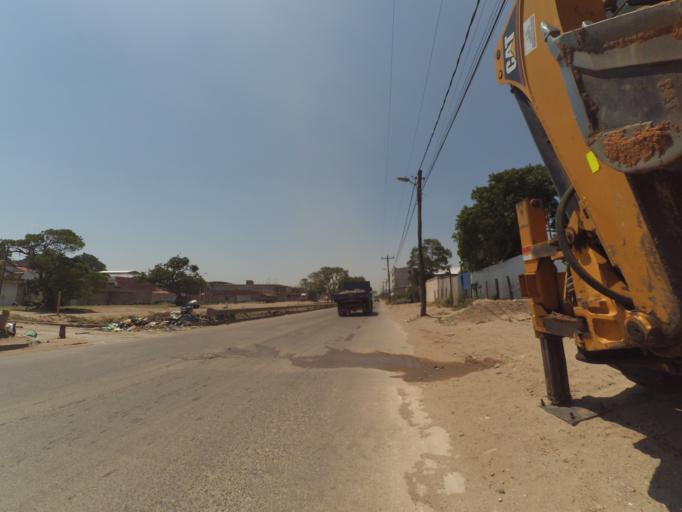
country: BO
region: Santa Cruz
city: Santa Cruz de la Sierra
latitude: -17.8345
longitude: -63.2401
